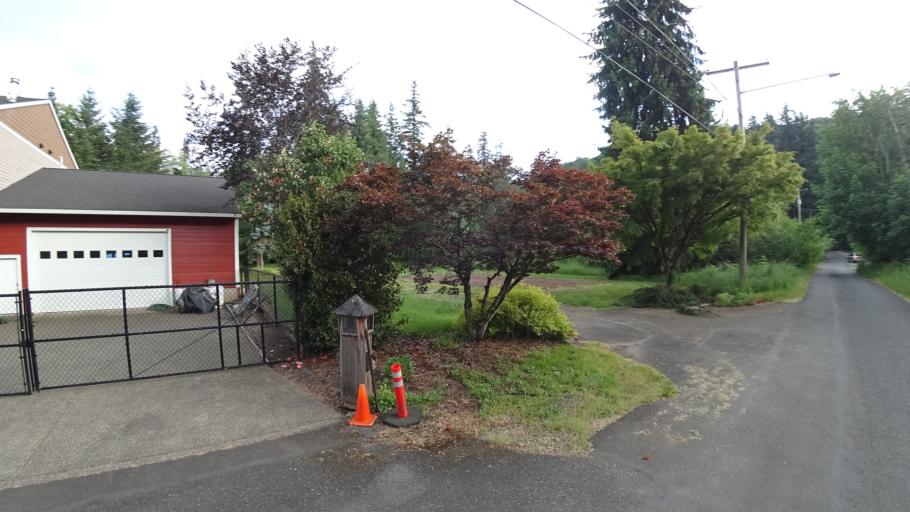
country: US
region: Oregon
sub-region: Clackamas County
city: Happy Valley
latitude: 45.4768
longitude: -122.4986
